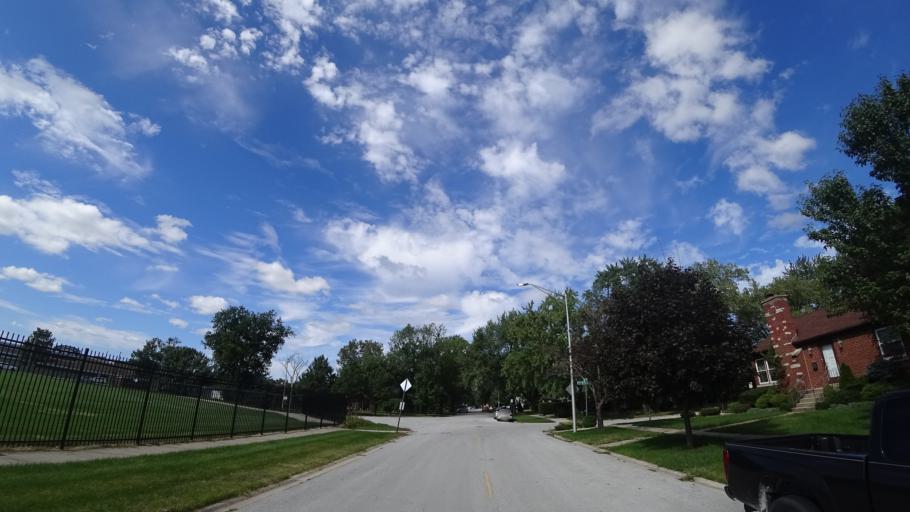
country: US
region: Illinois
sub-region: Cook County
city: Oak Lawn
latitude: 41.7212
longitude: -87.7653
